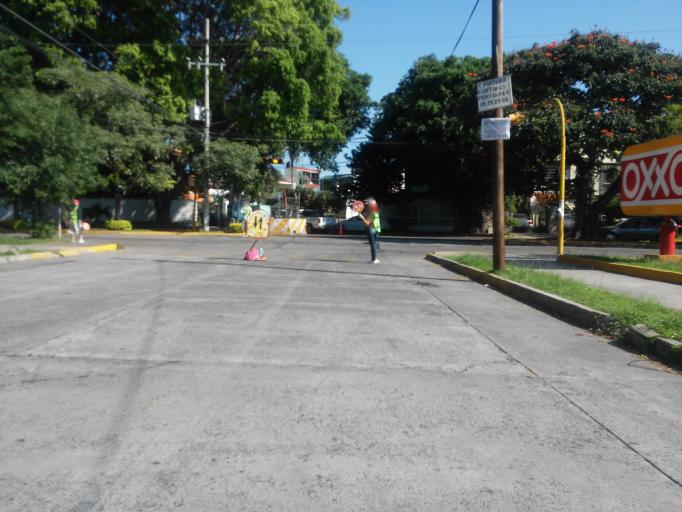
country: MX
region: Jalisco
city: Guadalajara
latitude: 20.6575
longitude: -103.3936
